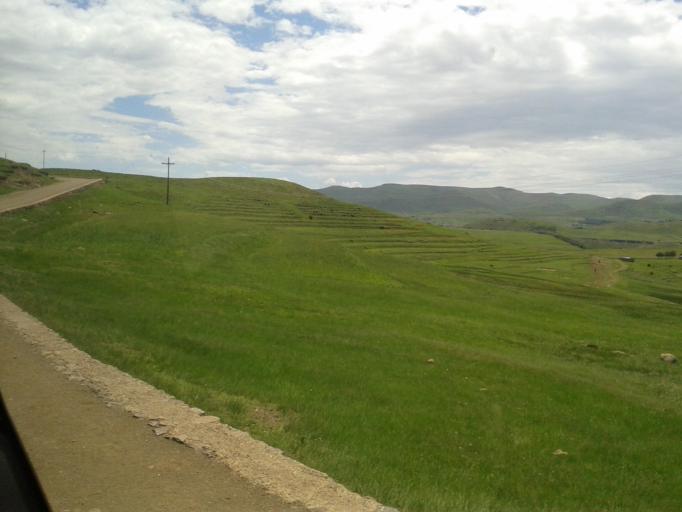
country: LS
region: Maseru
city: Nako
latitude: -29.8726
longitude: 28.0410
